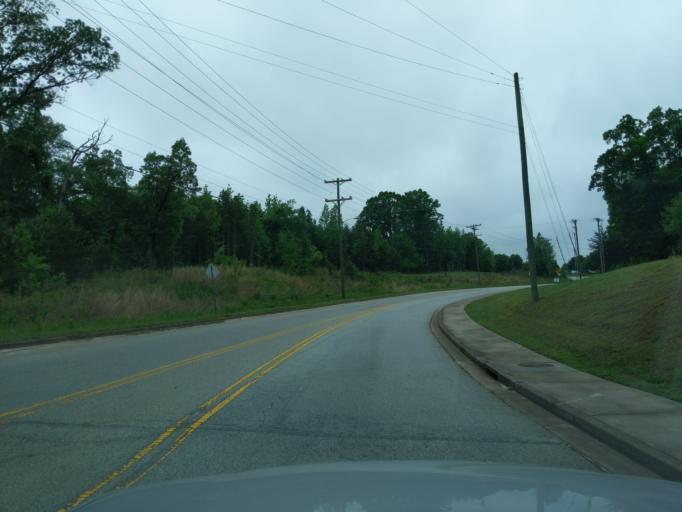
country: US
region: South Carolina
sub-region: Greenville County
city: Five Forks
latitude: 34.8621
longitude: -82.2165
